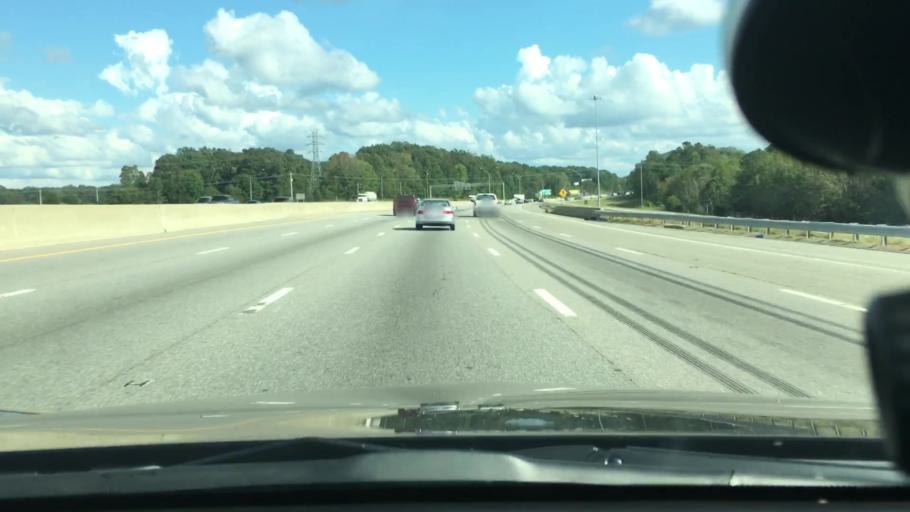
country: US
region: North Carolina
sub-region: Orange County
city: Hillsborough
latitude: 36.0728
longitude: -79.1605
